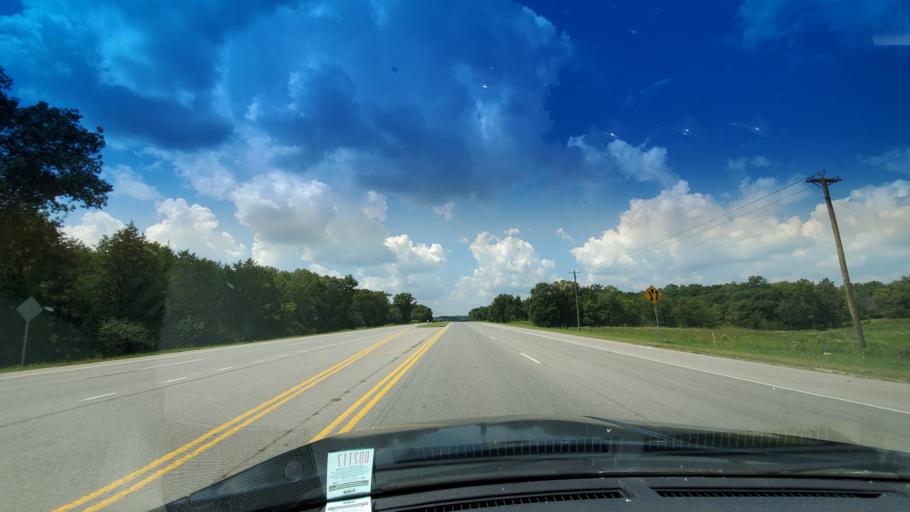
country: US
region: Tennessee
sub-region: Wilson County
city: Lebanon
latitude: 36.1752
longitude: -86.3139
